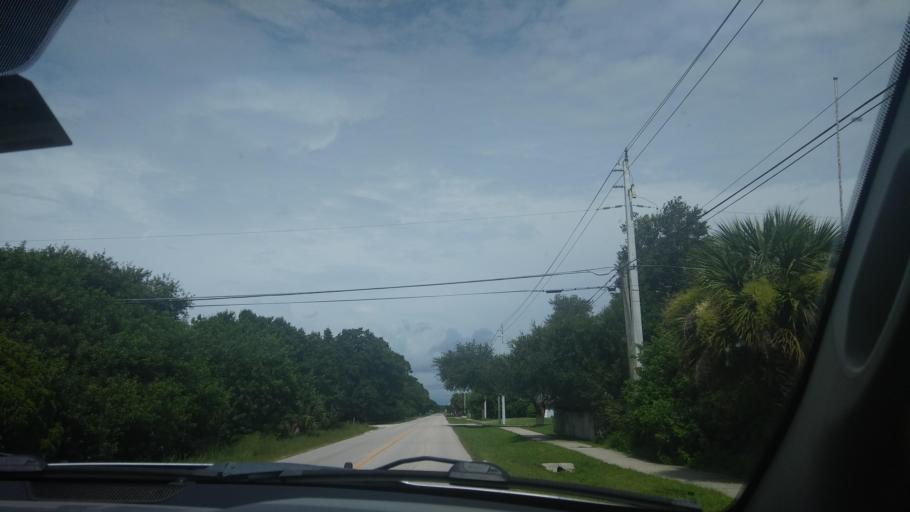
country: US
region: Florida
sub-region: Indian River County
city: Fellsmere
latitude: 27.7527
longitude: -80.5289
